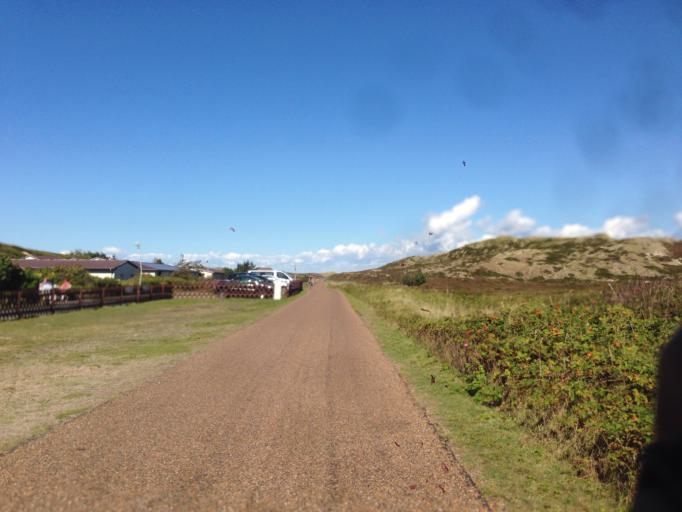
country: DE
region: Schleswig-Holstein
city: List
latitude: 54.9921
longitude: 8.3588
